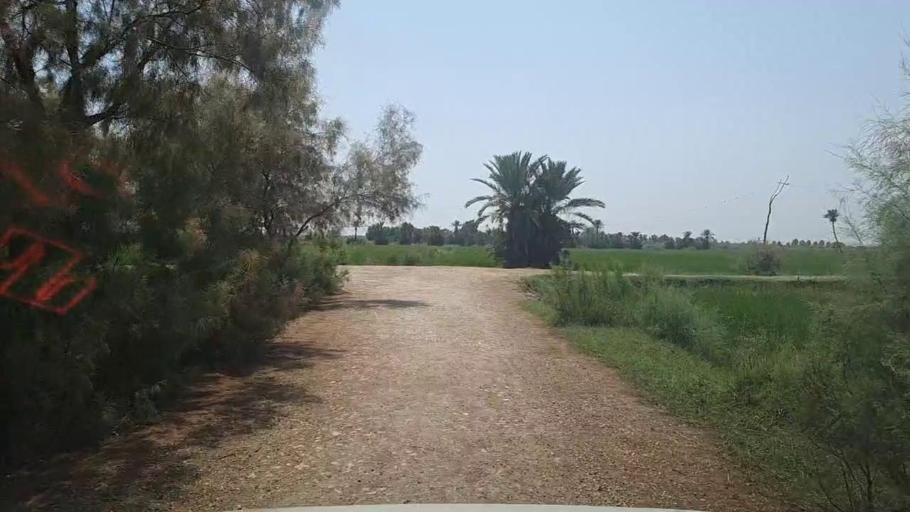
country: PK
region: Sindh
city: Kandhkot
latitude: 28.3066
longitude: 69.3566
